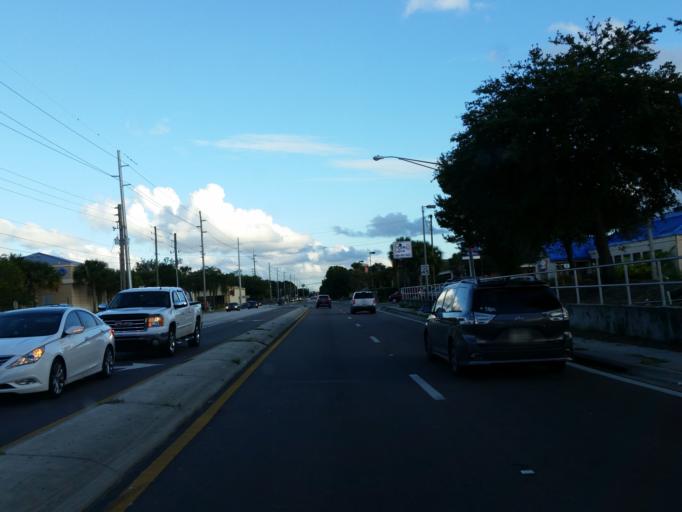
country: US
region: Florida
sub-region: Hillsborough County
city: Town 'n' Country
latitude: 27.9963
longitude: -82.5815
